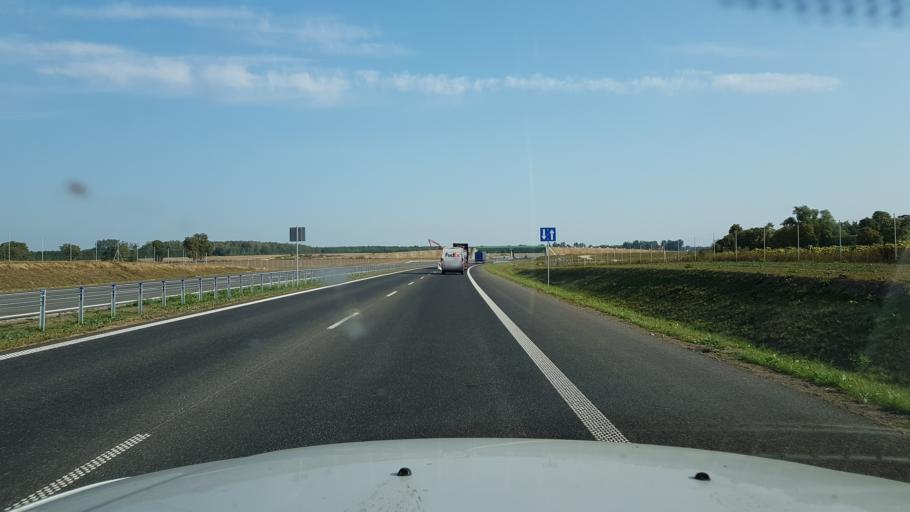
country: PL
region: West Pomeranian Voivodeship
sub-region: Powiat gryficki
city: Ploty
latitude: 53.7706
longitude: 15.2367
